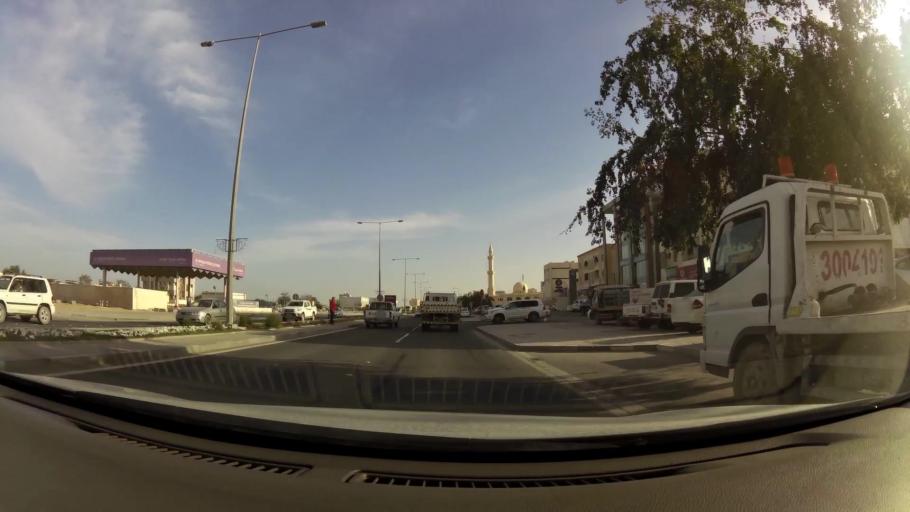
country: QA
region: Al Wakrah
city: Al Wakrah
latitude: 25.1697
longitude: 51.6074
